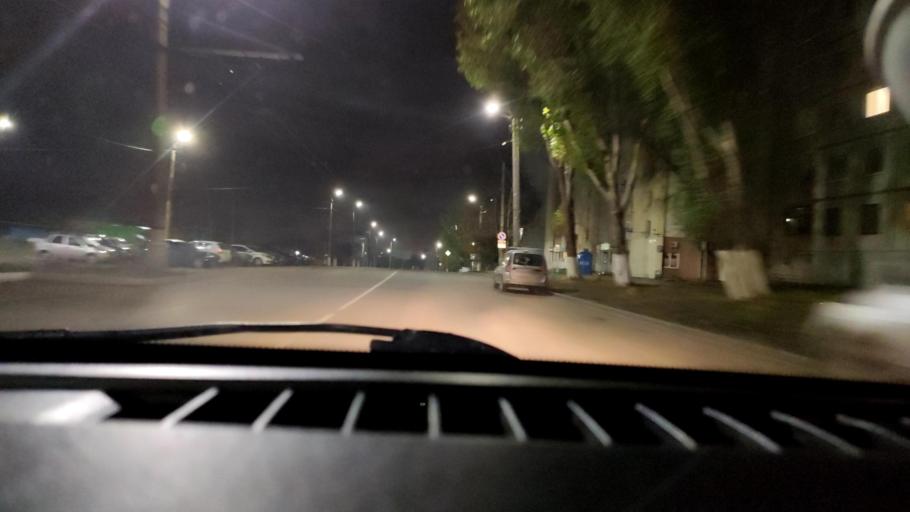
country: RU
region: Samara
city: Novokuybyshevsk
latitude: 53.1092
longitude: 49.9529
